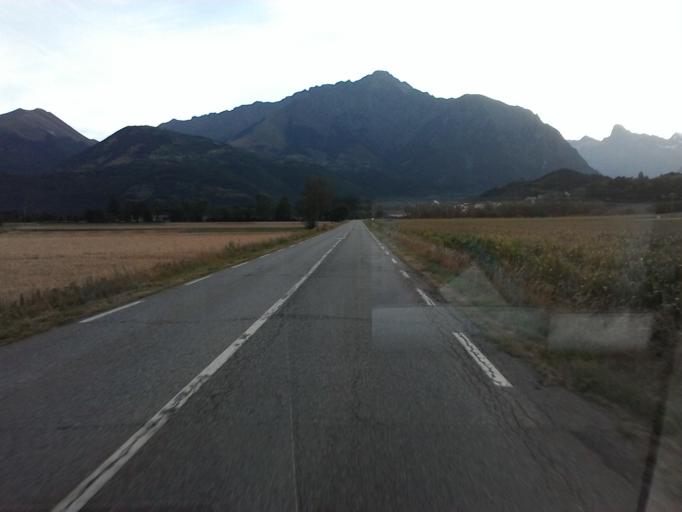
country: FR
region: Provence-Alpes-Cote d'Azur
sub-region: Departement des Hautes-Alpes
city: Saint-Bonnet-en-Champsaur
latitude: 44.7587
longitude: 6.0079
